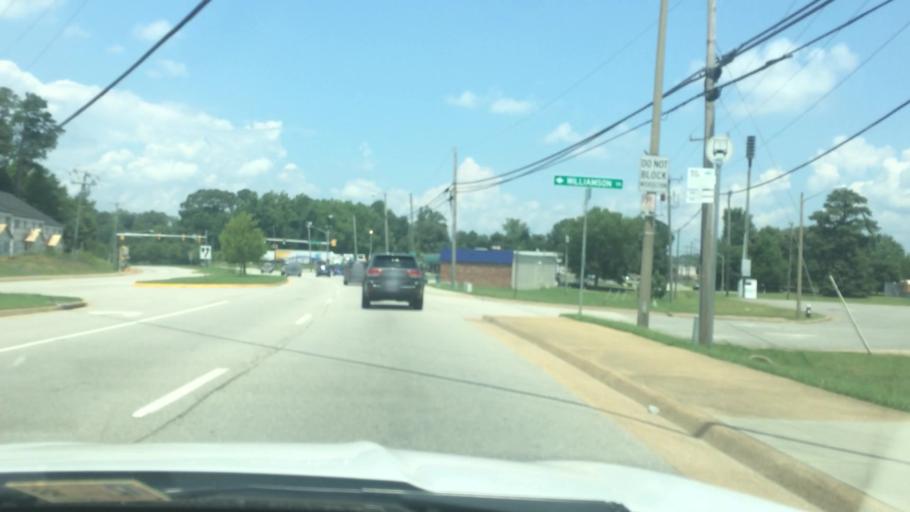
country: US
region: Virginia
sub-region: York County
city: Yorktown
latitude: 37.1629
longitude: -76.5569
